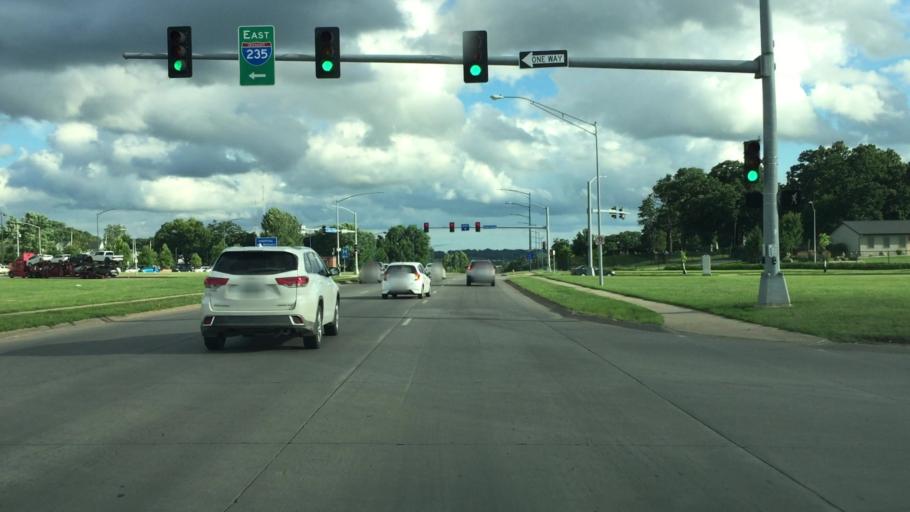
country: US
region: Iowa
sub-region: Polk County
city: Des Moines
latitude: 41.5953
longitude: -93.6444
